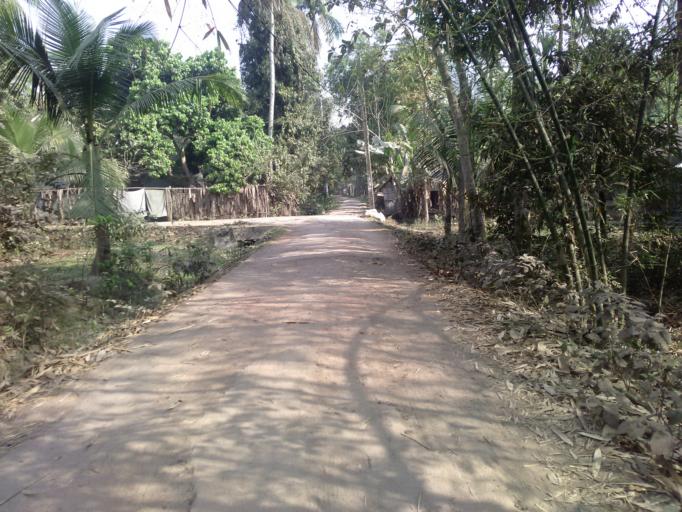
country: BD
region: Khulna
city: Khulna
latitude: 22.8974
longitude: 89.5280
